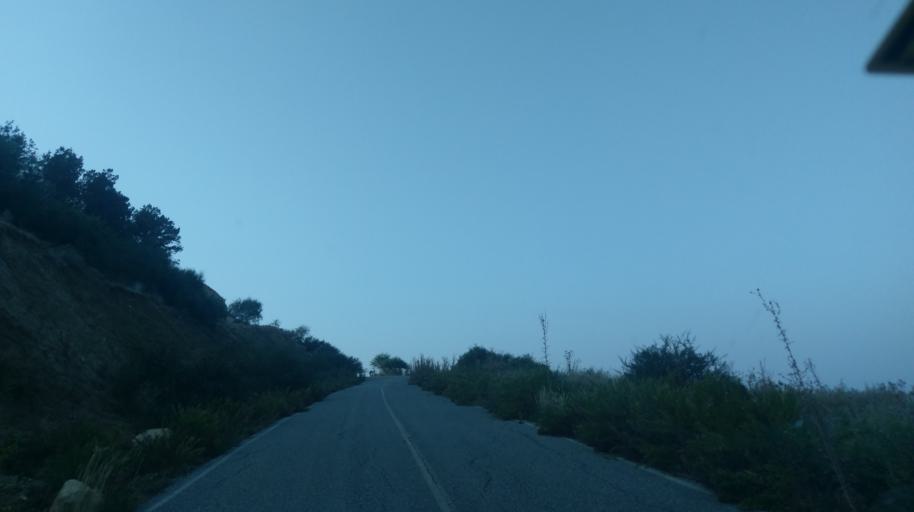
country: CY
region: Ammochostos
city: Trikomo
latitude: 35.4158
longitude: 33.9057
